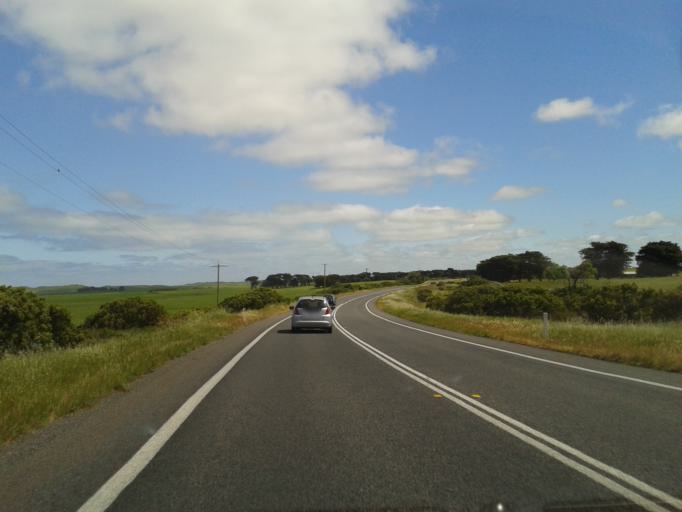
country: AU
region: Victoria
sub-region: Moyne
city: Port Fairy
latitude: -38.3483
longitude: 142.1131
